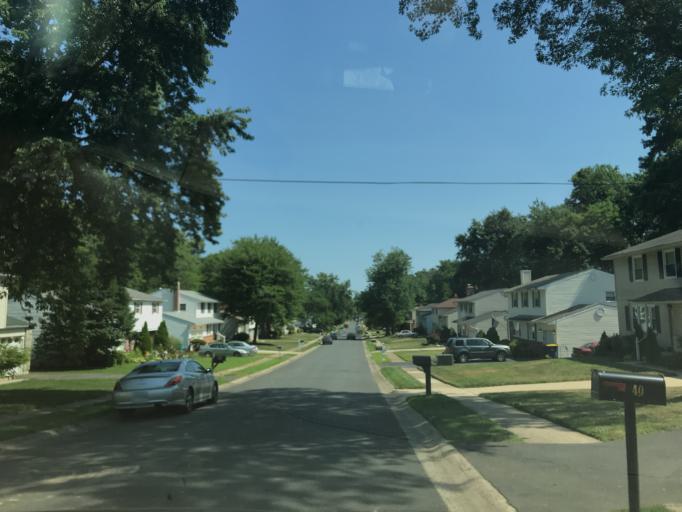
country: US
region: Delaware
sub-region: New Castle County
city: Claymont
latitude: 39.8347
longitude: -75.5185
